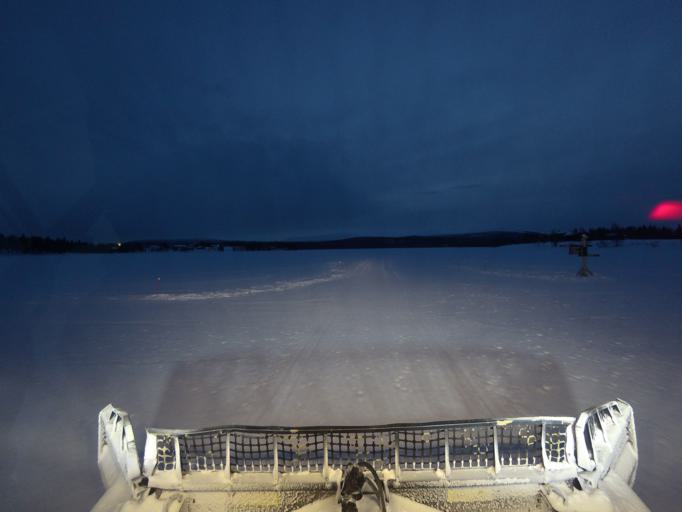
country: FI
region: Lapland
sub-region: Tunturi-Lappi
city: Kolari
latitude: 67.6088
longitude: 24.1442
